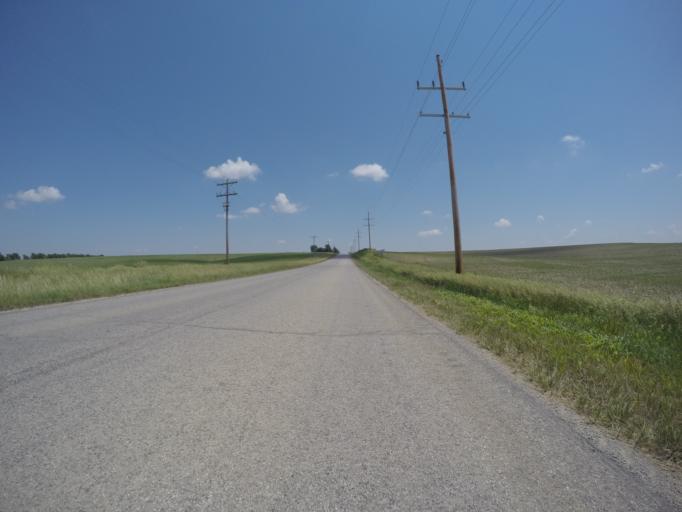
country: US
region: Kansas
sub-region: Doniphan County
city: Troy
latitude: 39.7689
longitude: -95.1141
